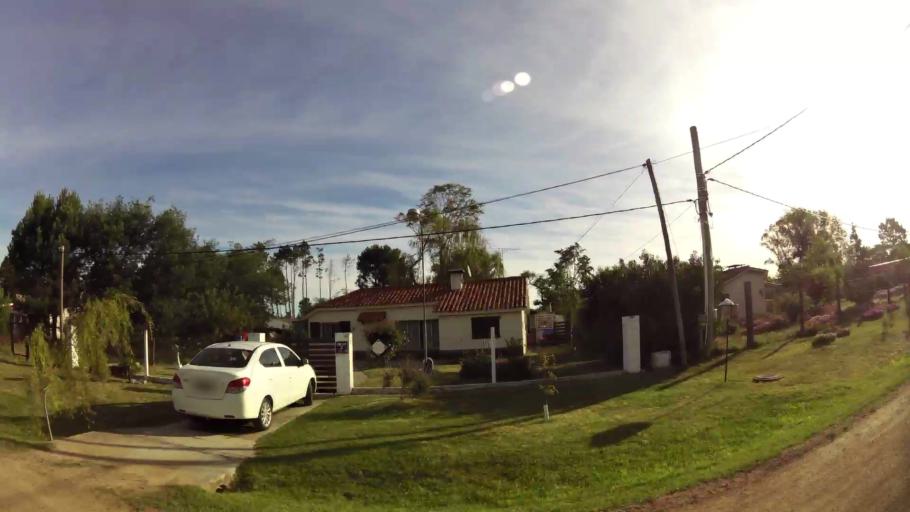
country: UY
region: Canelones
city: Empalme Olmos
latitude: -34.7859
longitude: -55.8592
